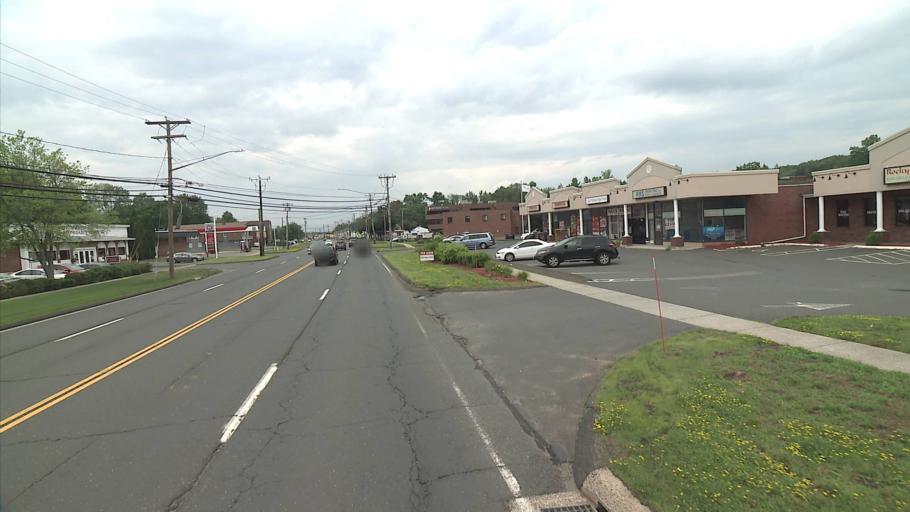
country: US
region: Connecticut
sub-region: Hartford County
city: Wethersfield
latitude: 41.6699
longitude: -72.6429
